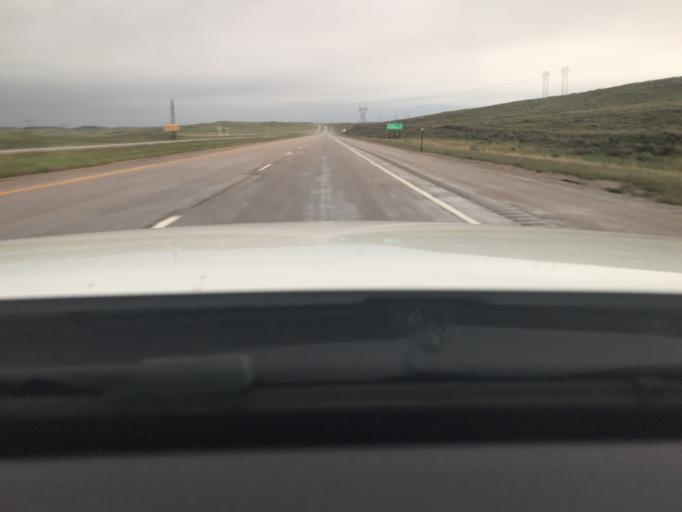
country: US
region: Wyoming
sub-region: Converse County
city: Glenrock
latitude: 42.8220
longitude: -105.7811
